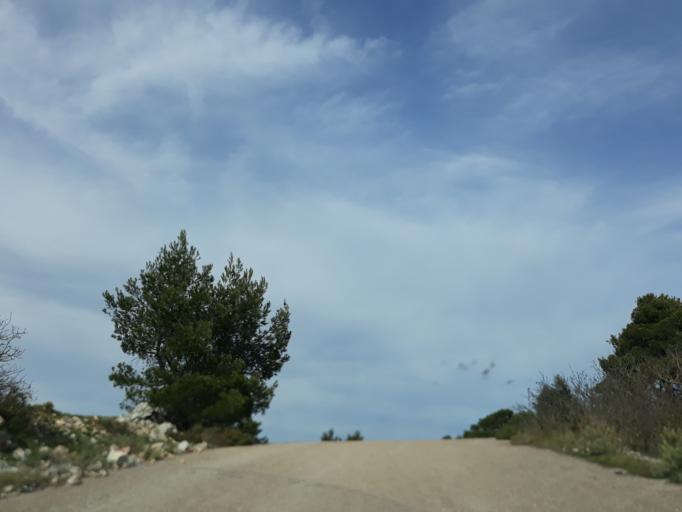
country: GR
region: Attica
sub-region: Nomarchia Anatolikis Attikis
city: Afidnes
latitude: 38.2174
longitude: 23.7928
